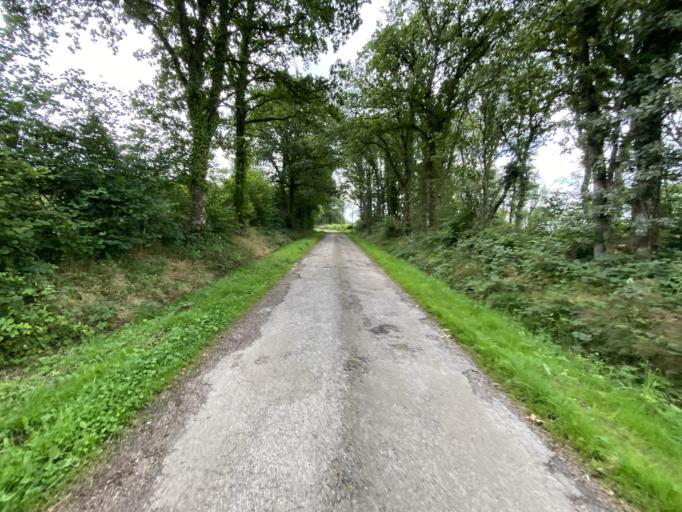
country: FR
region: Bourgogne
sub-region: Departement de la Cote-d'Or
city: Saulieu
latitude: 47.2843
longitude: 4.1743
